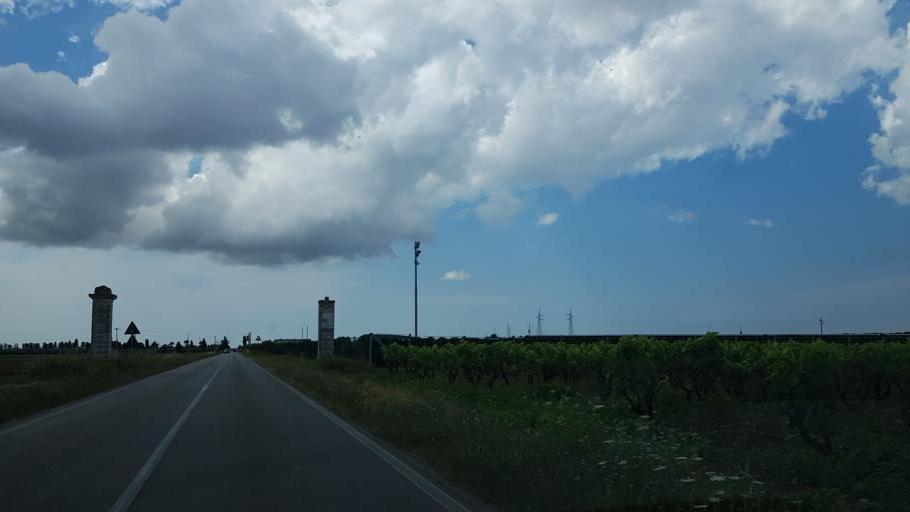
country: IT
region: Apulia
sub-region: Provincia di Brindisi
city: San Pancrazio Salentino
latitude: 40.3938
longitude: 17.8348
